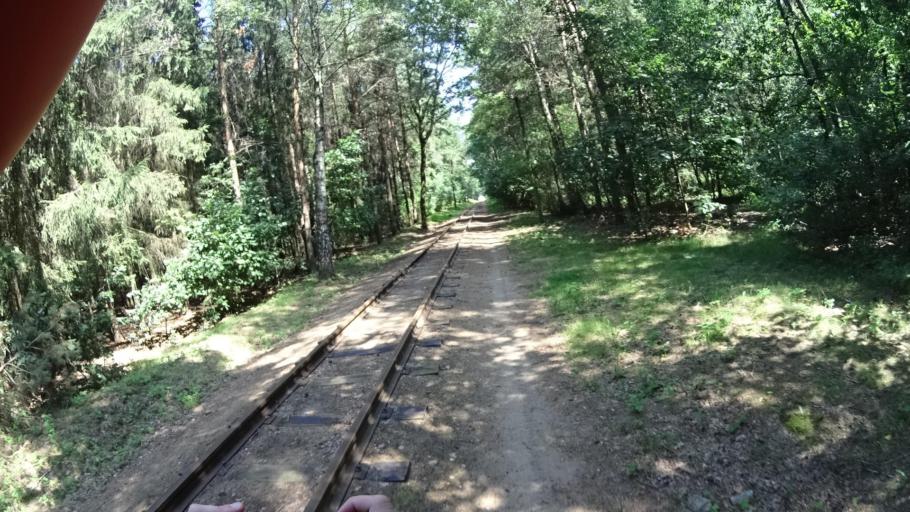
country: PL
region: Masovian Voivodeship
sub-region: Powiat piaseczynski
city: Tarczyn
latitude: 51.9944
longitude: 20.8951
